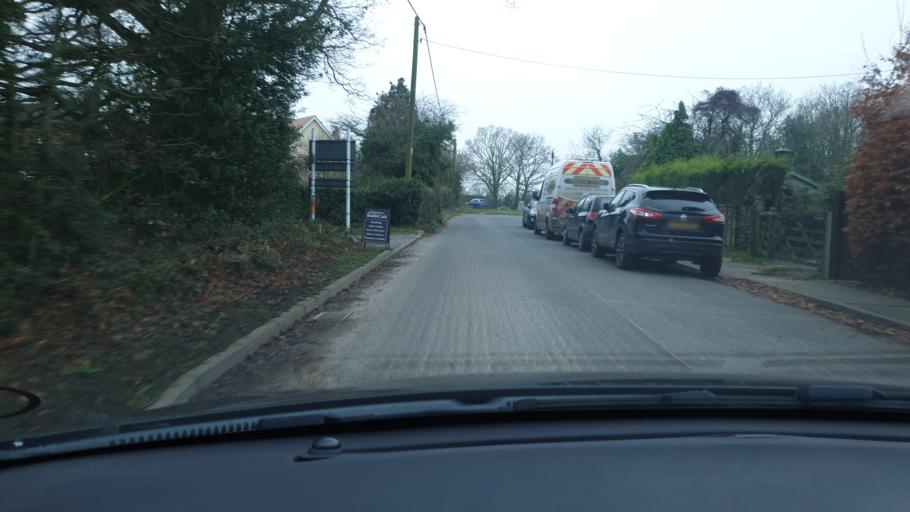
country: GB
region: England
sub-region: Essex
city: Great Bentley
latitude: 51.8392
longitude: 1.0716
